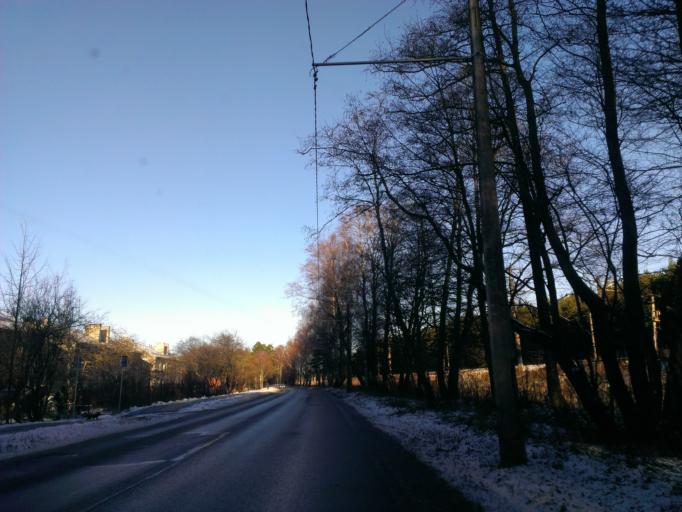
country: LV
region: Riga
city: Bolderaja
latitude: 57.0608
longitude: 24.1063
